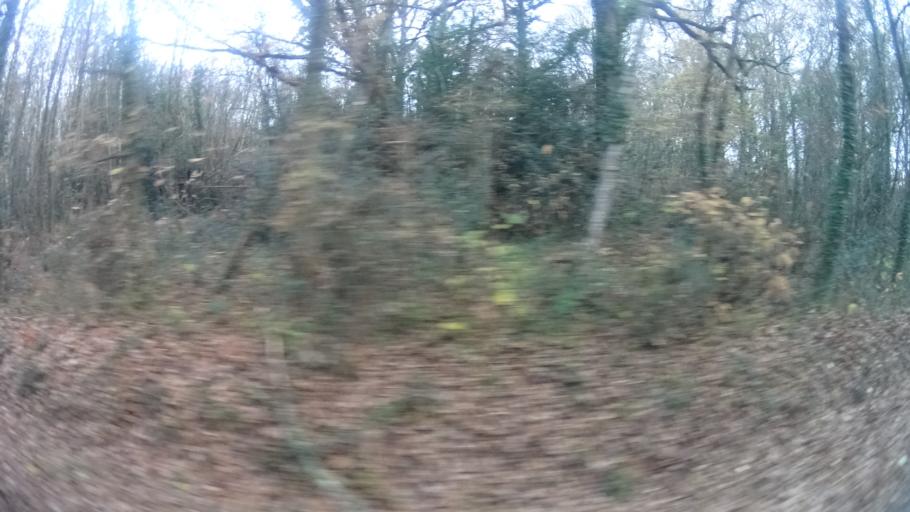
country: FR
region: Pays de la Loire
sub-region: Departement de la Loire-Atlantique
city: Avessac
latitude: 47.6498
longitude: -2.0208
